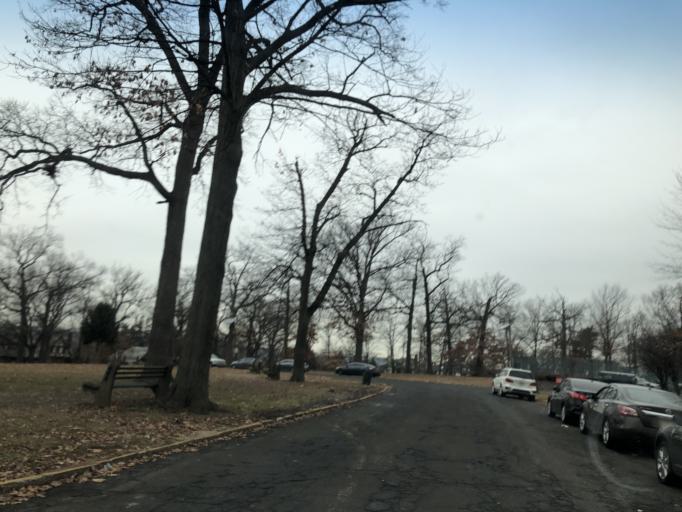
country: US
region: New Jersey
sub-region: Bergen County
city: Elmwood Park
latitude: 40.9168
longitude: -74.1375
